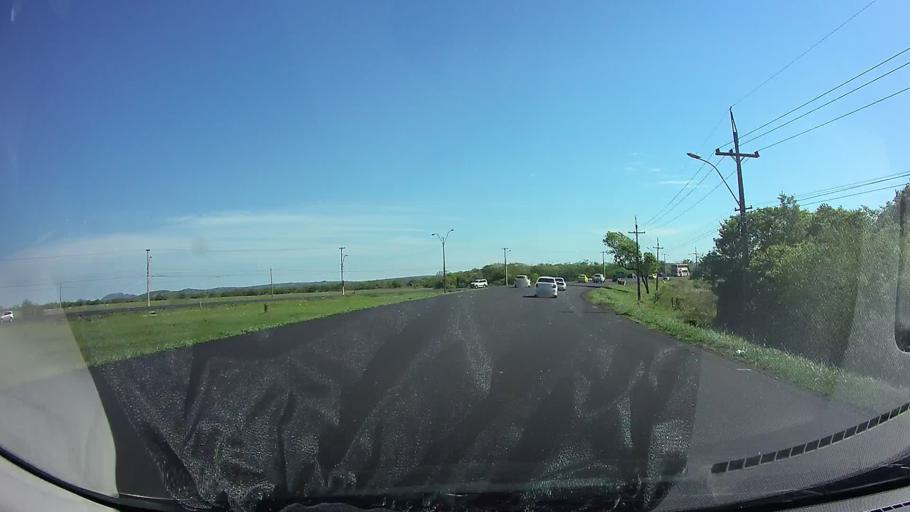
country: PY
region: Central
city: Ypacarai
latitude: -25.3869
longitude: -57.2665
